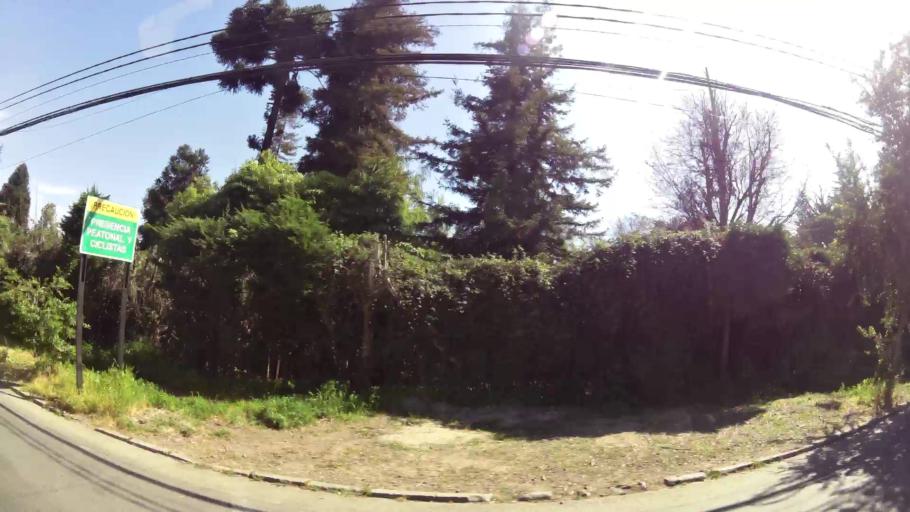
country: CL
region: Santiago Metropolitan
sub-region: Provincia de Santiago
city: Villa Presidente Frei, Nunoa, Santiago, Chile
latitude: -33.4341
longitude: -70.5203
